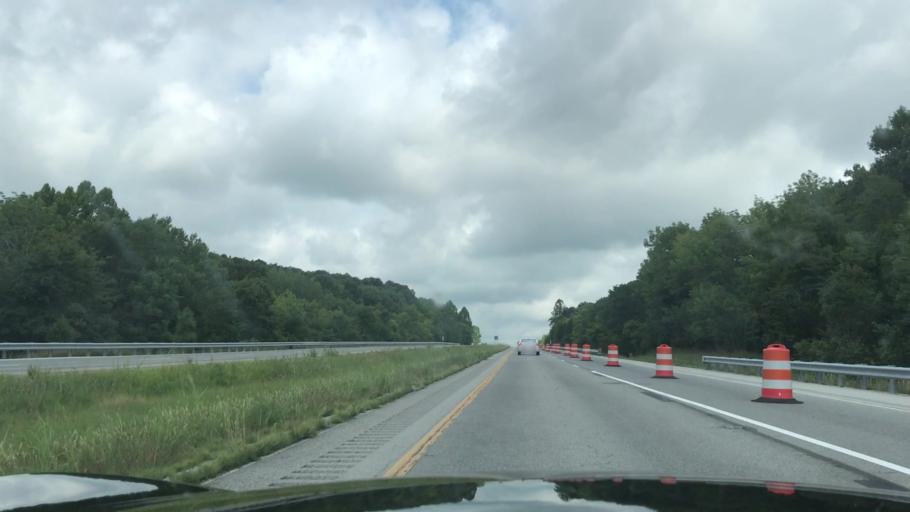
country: US
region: Kentucky
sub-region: Butler County
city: Morgantown
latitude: 37.0942
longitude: -86.6304
